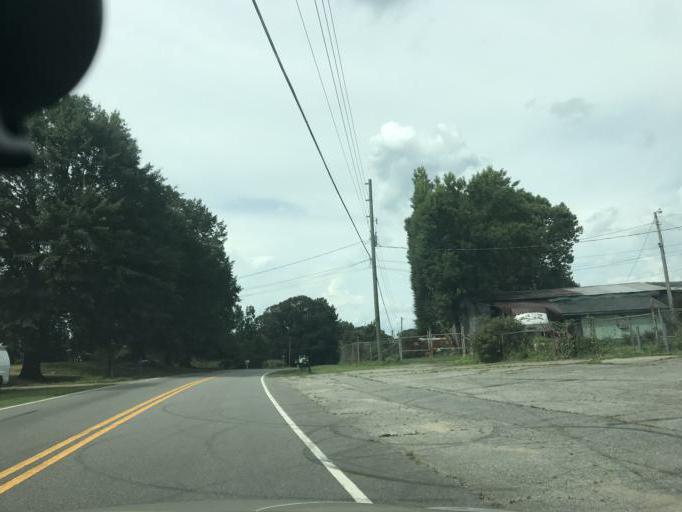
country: US
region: Georgia
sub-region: Forsyth County
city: Cumming
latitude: 34.2648
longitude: -84.2378
